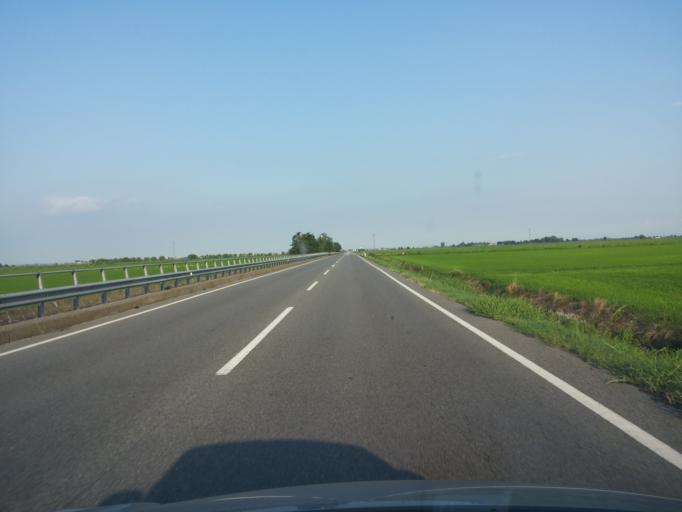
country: IT
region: Piedmont
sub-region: Provincia di Vercelli
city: Olcenengo
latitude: 45.3357
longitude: 8.3043
